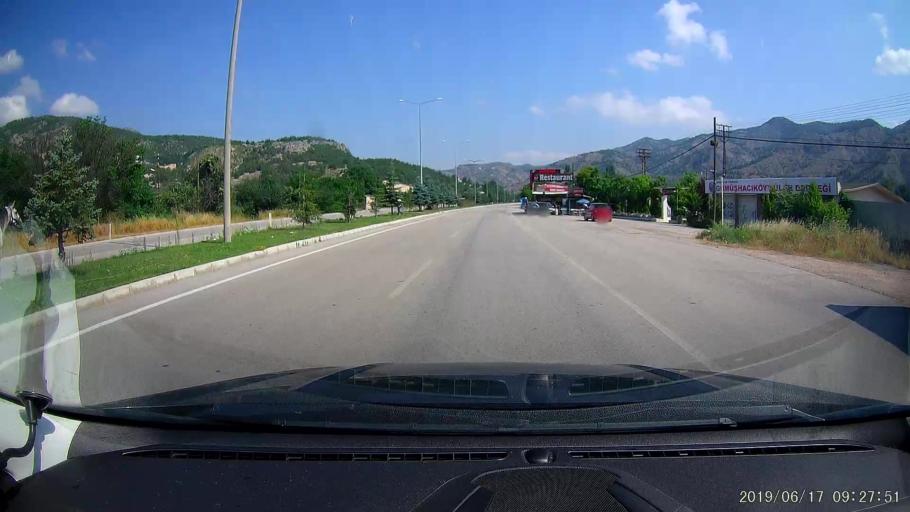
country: TR
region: Amasya
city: Amasya
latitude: 40.6816
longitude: 35.8240
